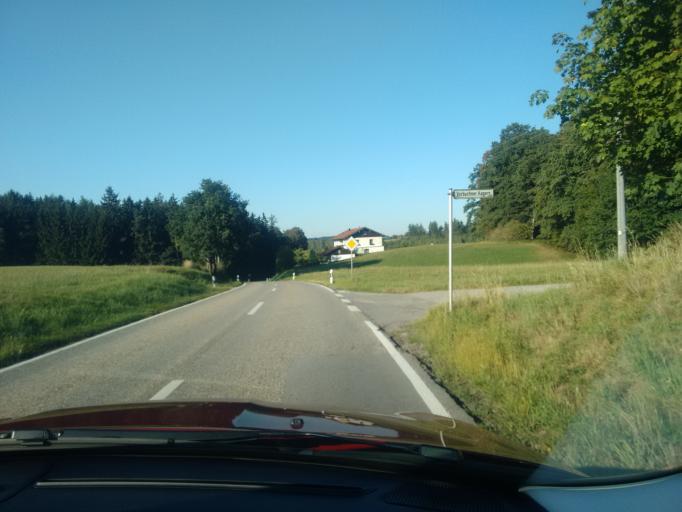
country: DE
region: Bavaria
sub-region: Upper Bavaria
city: Halsbach
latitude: 48.1234
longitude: 12.7199
